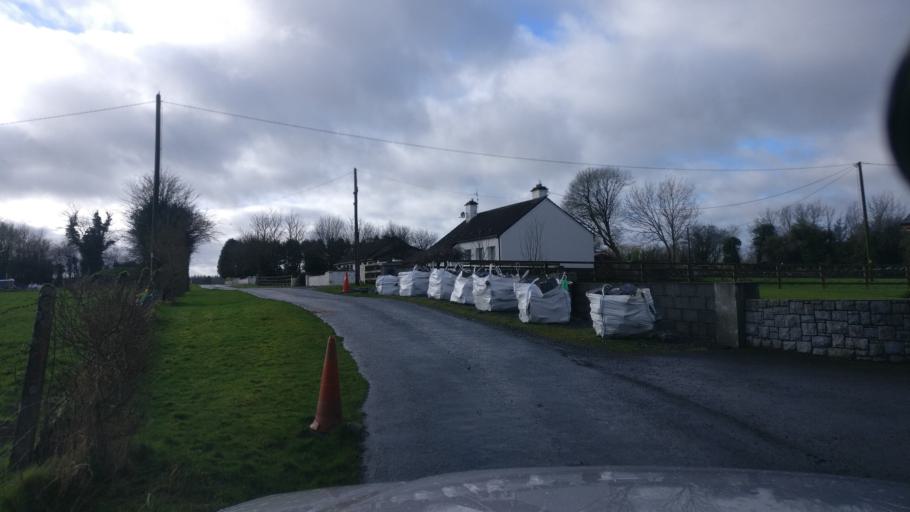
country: IE
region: Connaught
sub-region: County Galway
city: Loughrea
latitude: 53.2440
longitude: -8.6374
